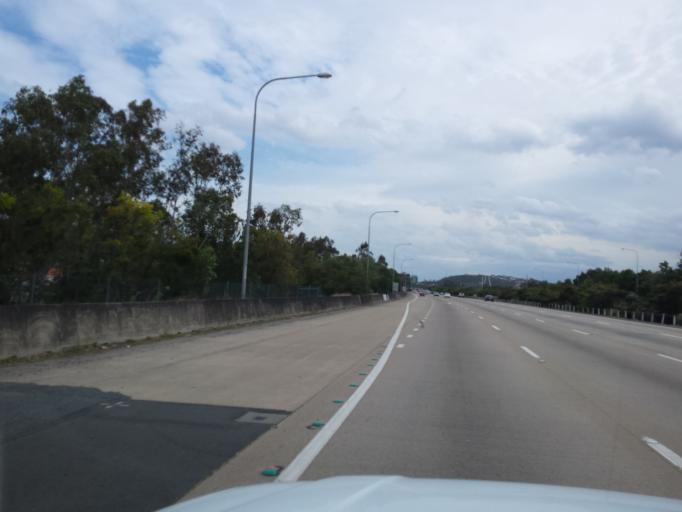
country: AU
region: Queensland
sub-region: Gold Coast
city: Oxenford
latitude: -27.9000
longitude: 153.3152
